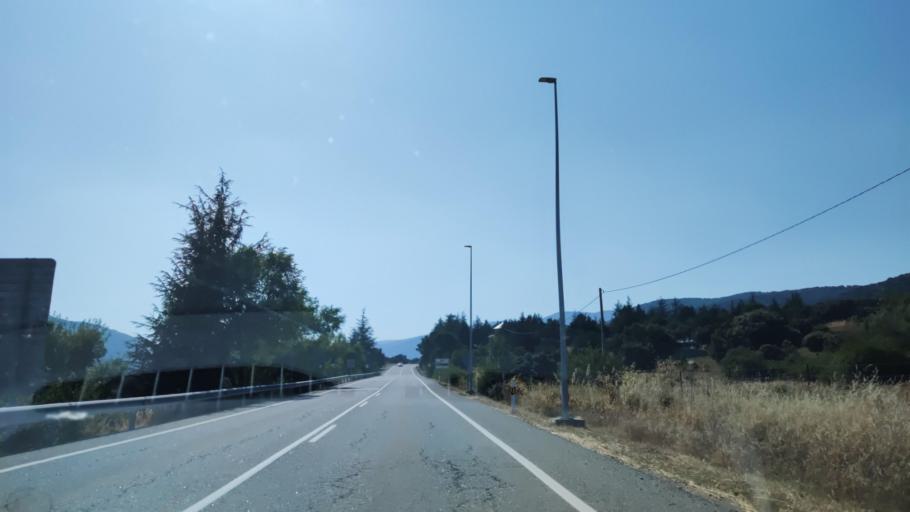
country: ES
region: Madrid
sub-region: Provincia de Madrid
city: Canencia
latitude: 40.9448
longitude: -3.7258
